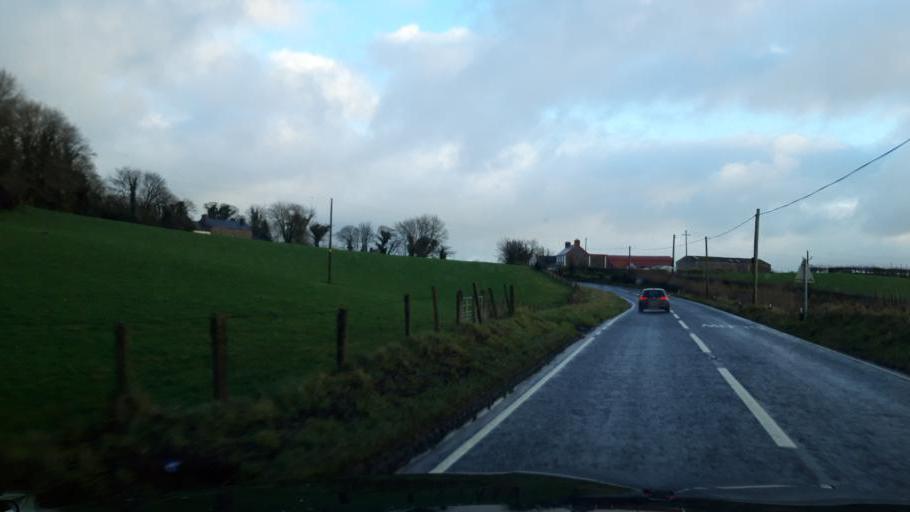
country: GB
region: Northern Ireland
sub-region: Moyle District
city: Ballycastle
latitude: 55.1802
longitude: -6.2890
